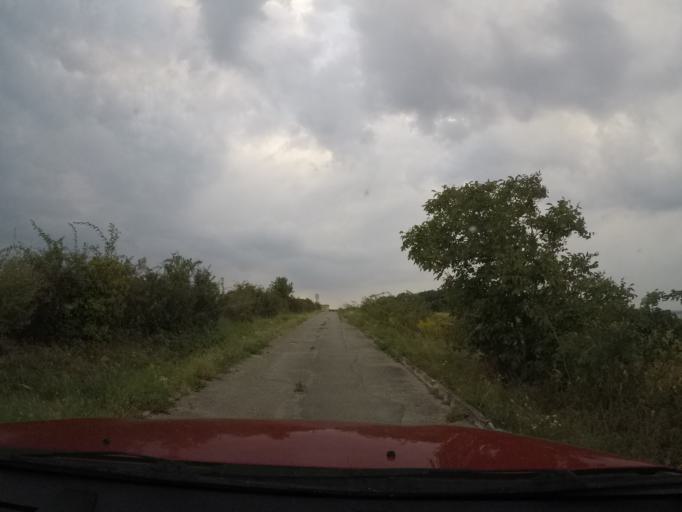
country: SK
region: Kosicky
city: Kosice
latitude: 48.6916
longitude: 21.2214
